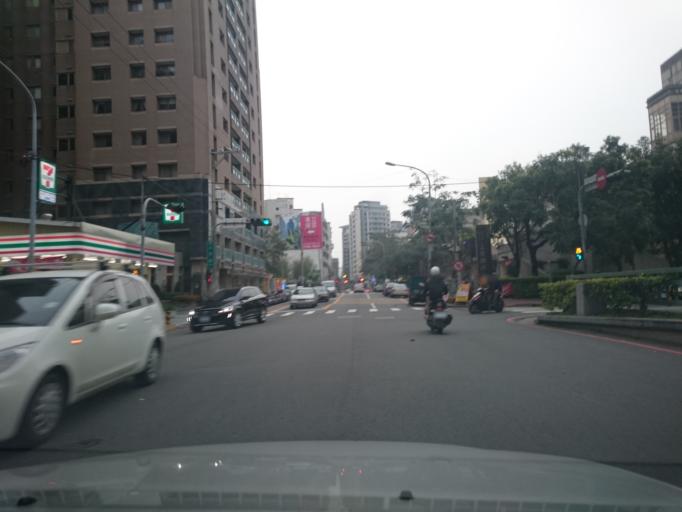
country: TW
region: Taiwan
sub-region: Taichung City
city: Taichung
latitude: 24.1717
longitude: 120.6395
